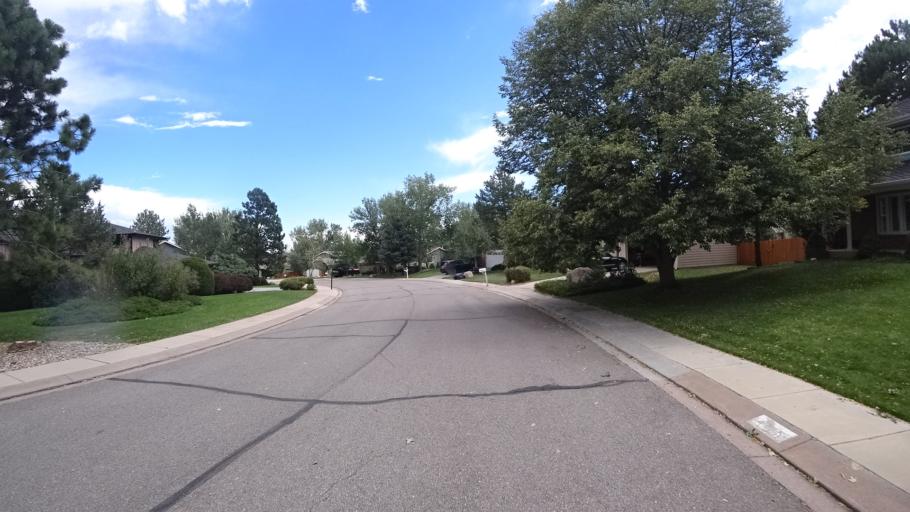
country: US
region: Colorado
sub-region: El Paso County
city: Stratmoor
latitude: 38.7716
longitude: -104.8166
